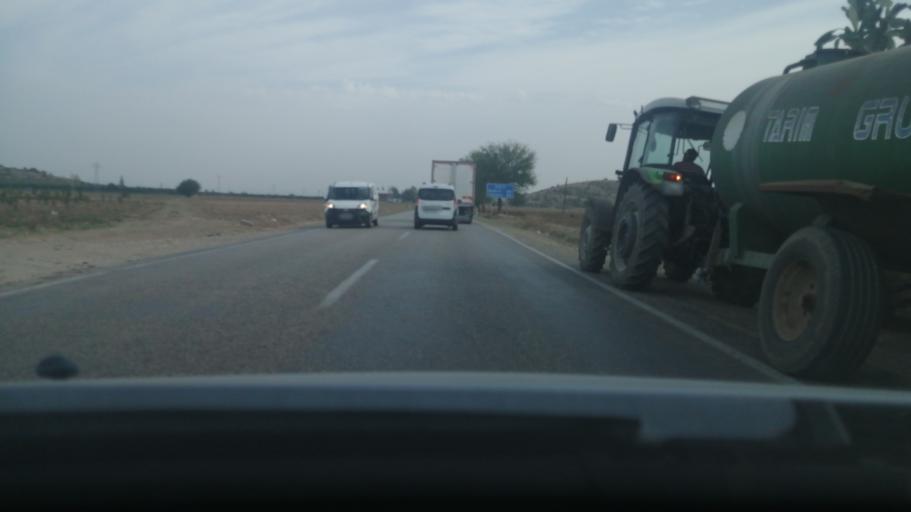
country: TR
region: Adana
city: Kozan
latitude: 37.3733
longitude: 35.8397
